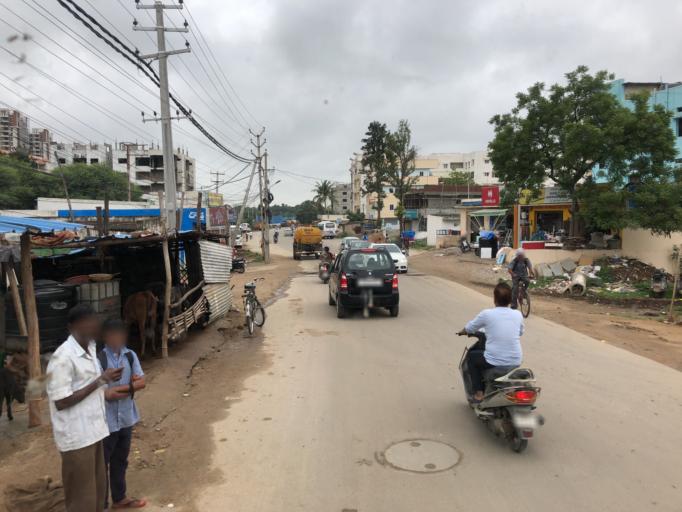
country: IN
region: Telangana
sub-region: Medak
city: Serilingampalle
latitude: 17.4660
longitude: 78.3408
